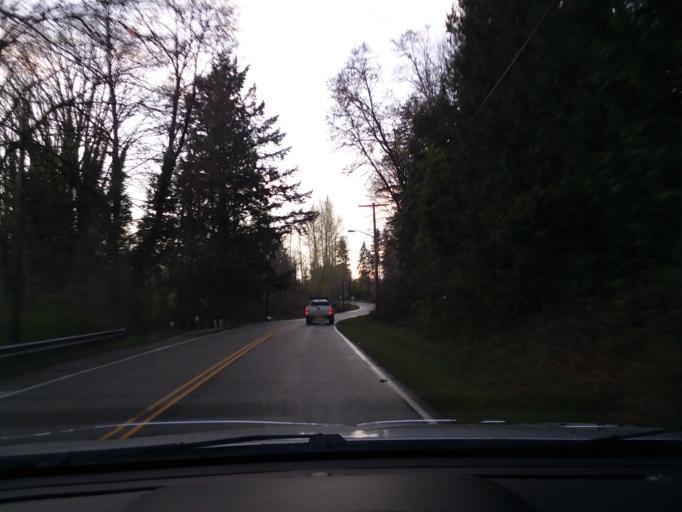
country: US
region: Washington
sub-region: King County
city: Kenmore
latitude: 47.7707
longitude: -122.2425
